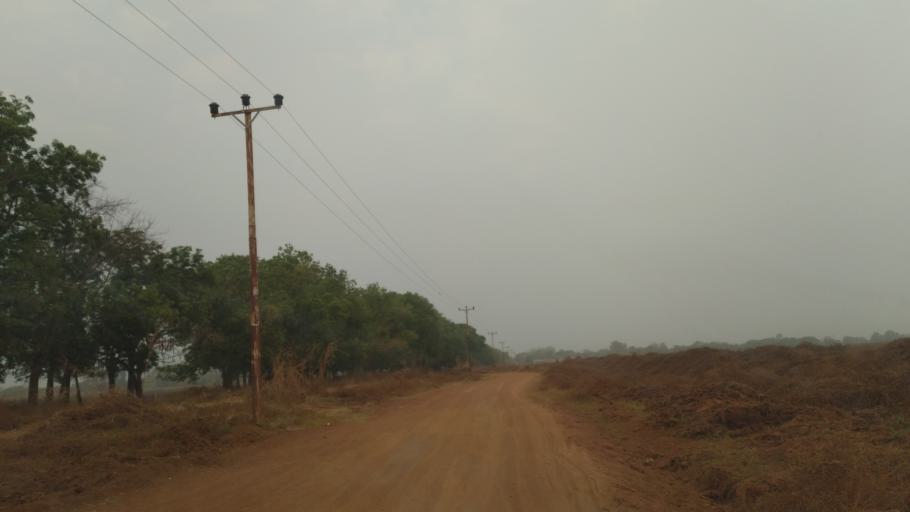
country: ET
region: Gambela
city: Gambela
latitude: 7.8955
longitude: 34.5518
